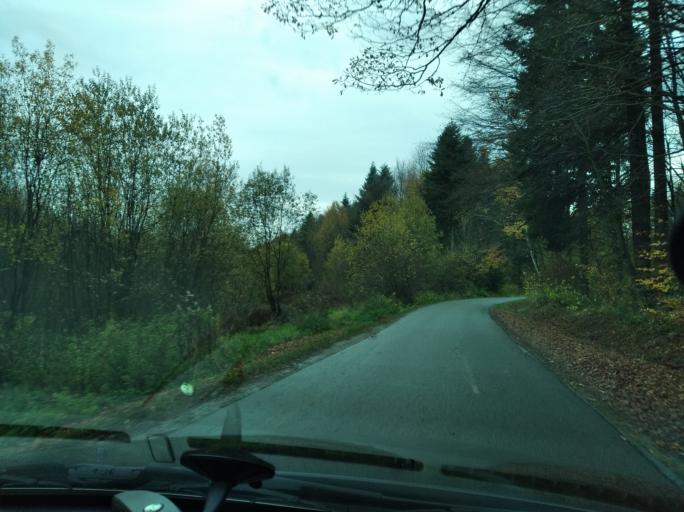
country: PL
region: Subcarpathian Voivodeship
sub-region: Powiat strzyzowski
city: Strzyzow
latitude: 49.9076
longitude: 21.7816
